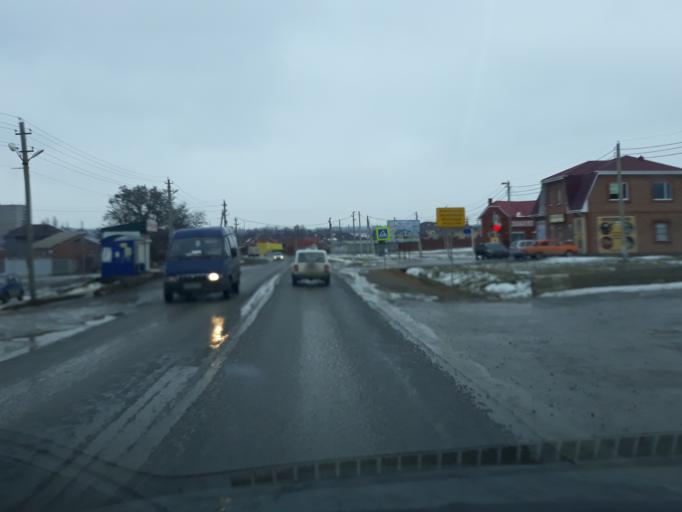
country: RU
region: Rostov
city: Krym
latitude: 47.2836
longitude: 39.5191
